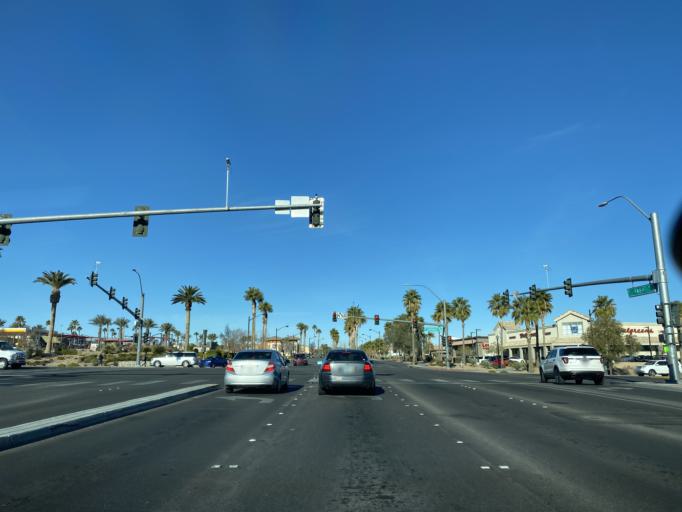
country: US
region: Nevada
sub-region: Clark County
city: Summerlin South
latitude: 36.3009
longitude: -115.2823
